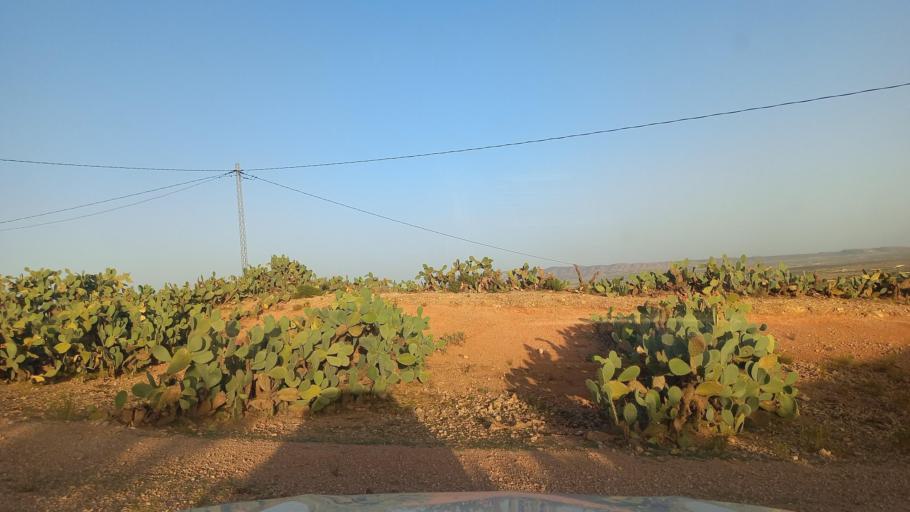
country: TN
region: Al Qasrayn
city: Sbiba
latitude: 35.3738
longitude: 9.0046
